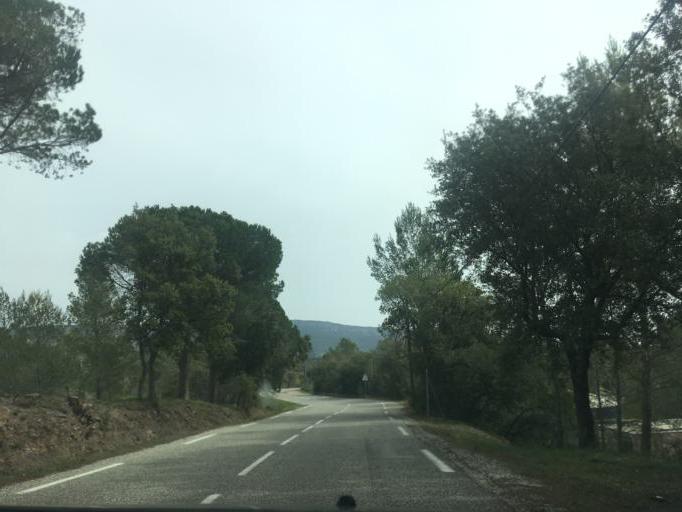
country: FR
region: Provence-Alpes-Cote d'Azur
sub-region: Departement du Var
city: Le Muy
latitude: 43.5012
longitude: 6.5824
